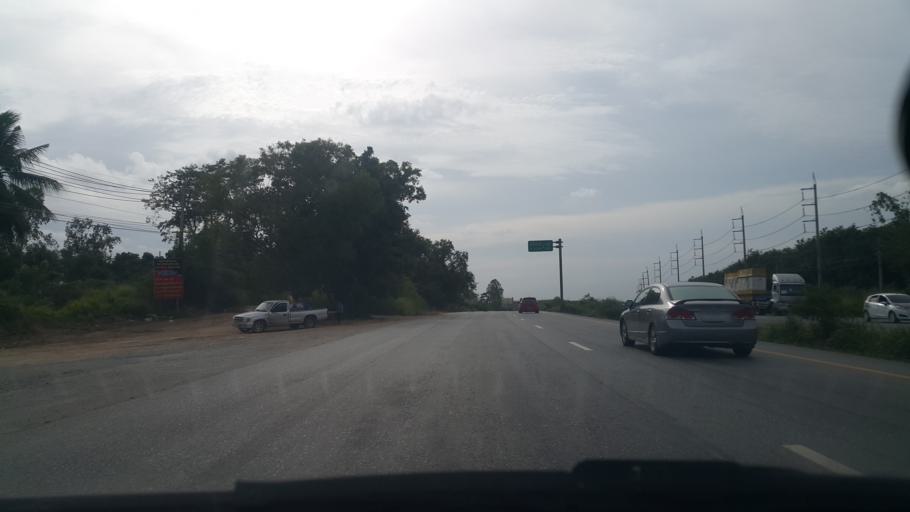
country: TH
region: Rayong
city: Nikhom Phattana
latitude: 12.8691
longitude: 101.0688
